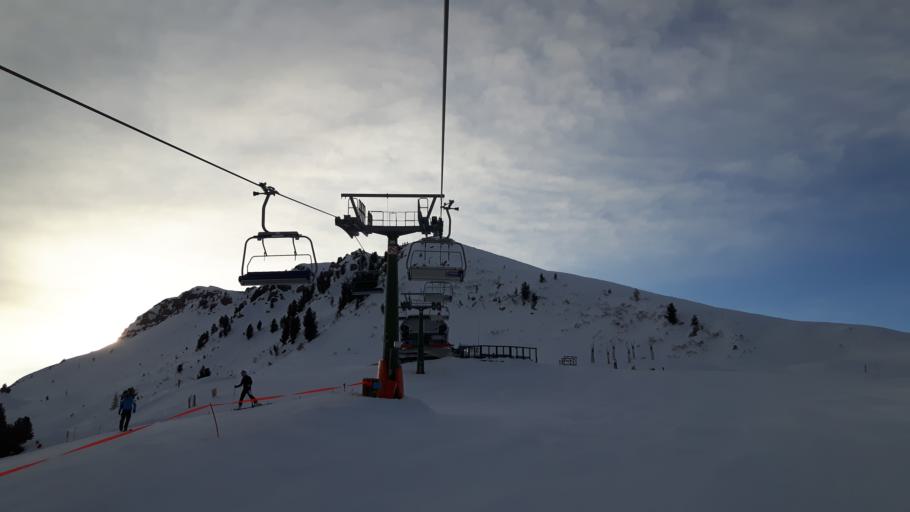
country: IT
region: Trentino-Alto Adige
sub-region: Provincia di Trento
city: Panchia
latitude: 46.3346
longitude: 11.5470
